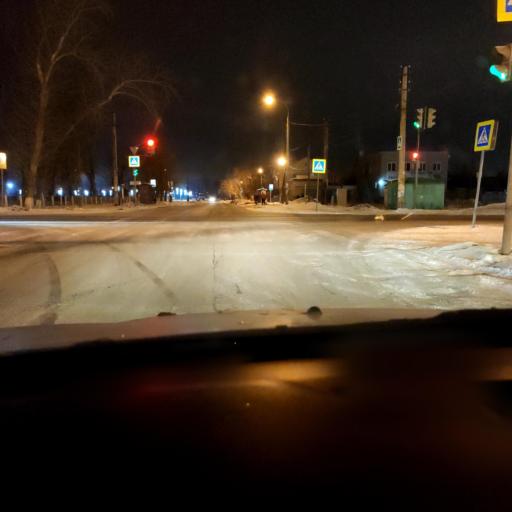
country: RU
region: Samara
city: Petra-Dubrava
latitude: 53.2520
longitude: 50.3385
